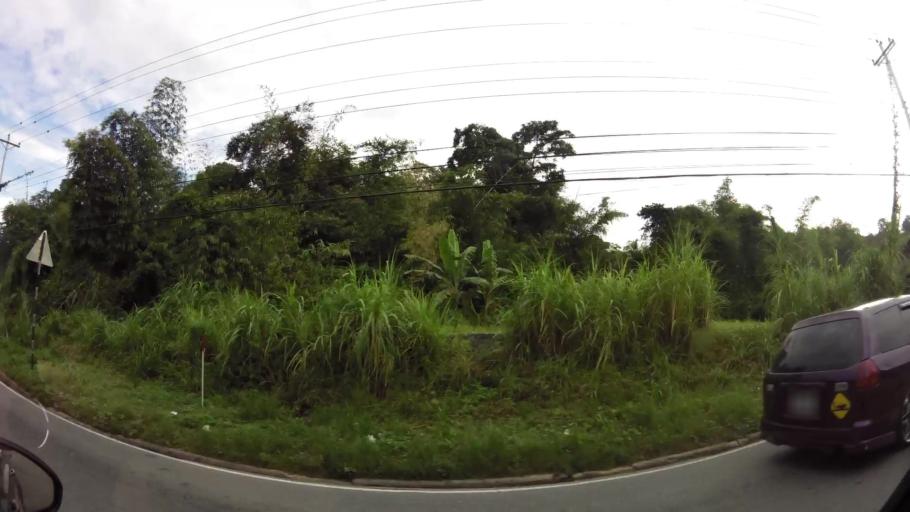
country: TT
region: San Juan/Laventille
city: Laventille
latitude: 10.6575
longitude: -61.4466
